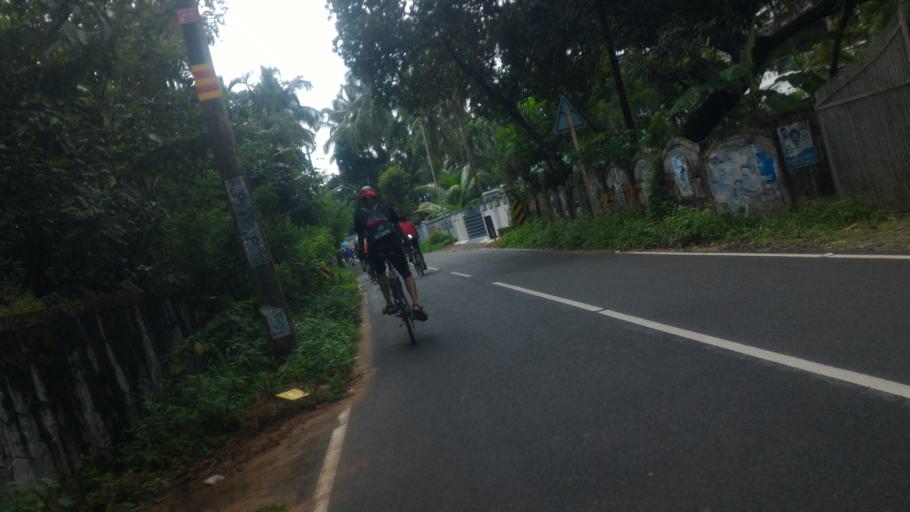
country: IN
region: Kerala
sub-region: Thrissur District
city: Thanniyam
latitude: 10.4386
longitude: 76.0828
